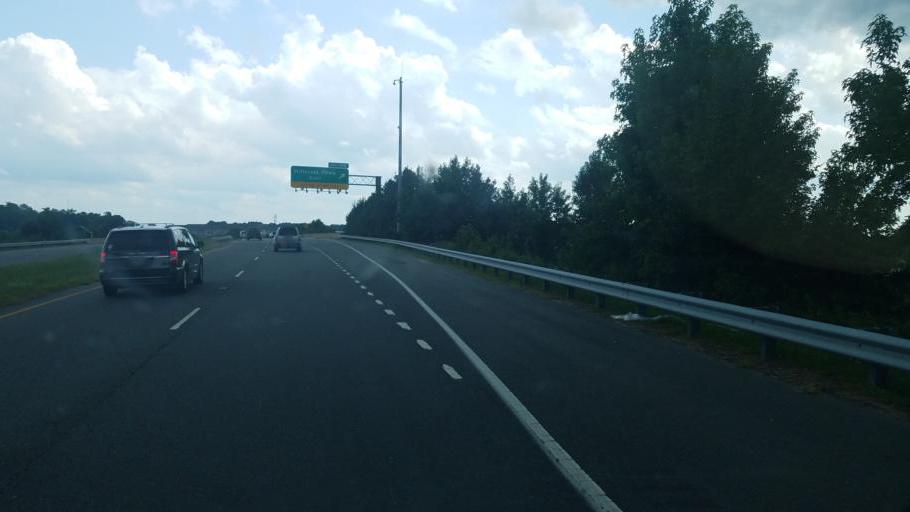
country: US
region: North Carolina
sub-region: Currituck County
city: Moyock
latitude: 36.6588
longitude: -76.2302
